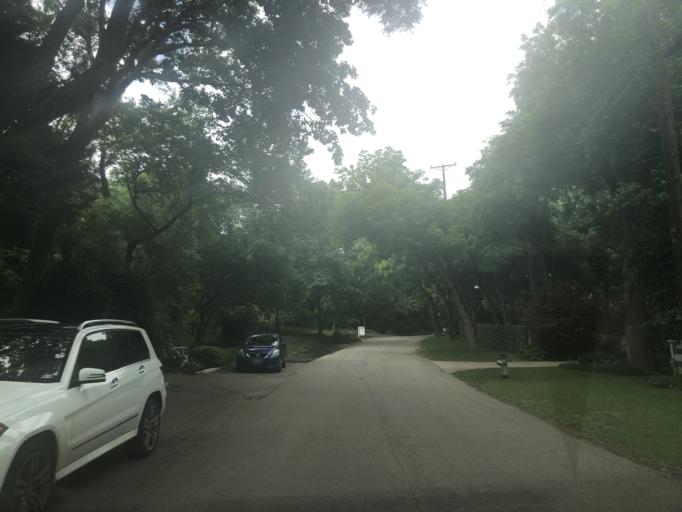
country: US
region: Texas
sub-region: Dallas County
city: University Park
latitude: 32.8605
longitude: -96.8350
